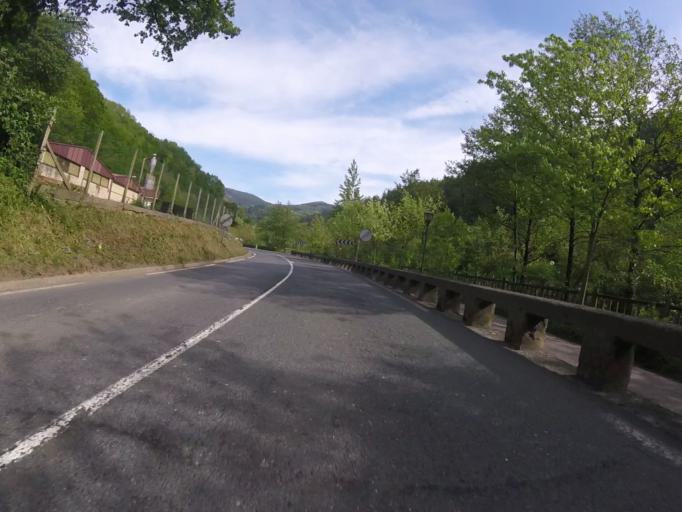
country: ES
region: Basque Country
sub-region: Provincia de Guipuzcoa
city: Urretxu
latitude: 43.1035
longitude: -2.3169
